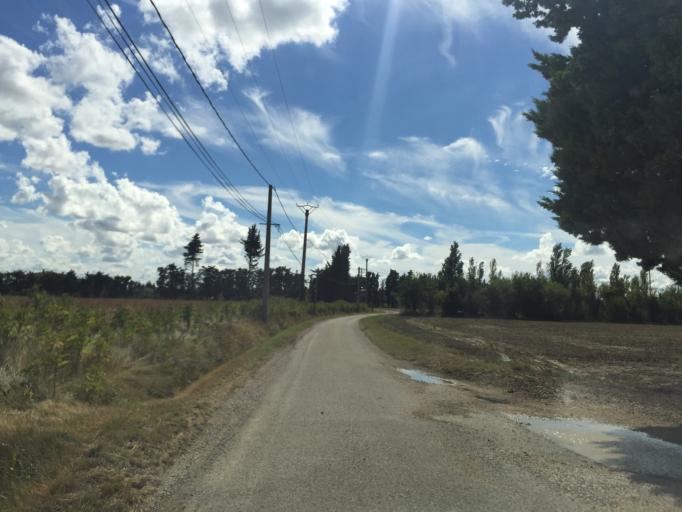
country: FR
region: Provence-Alpes-Cote d'Azur
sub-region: Departement du Vaucluse
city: Caderousse
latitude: 44.1199
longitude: 4.7367
